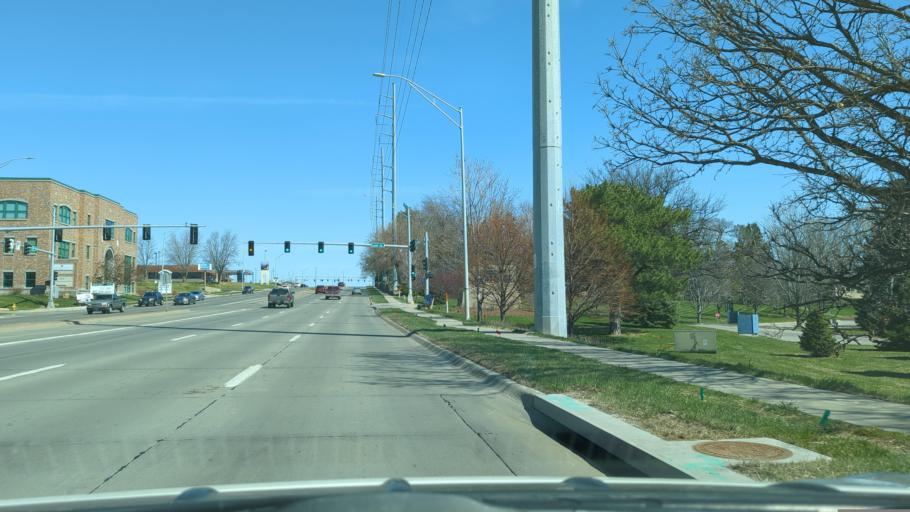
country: US
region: Nebraska
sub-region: Douglas County
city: Ralston
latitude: 41.2395
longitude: -96.0239
